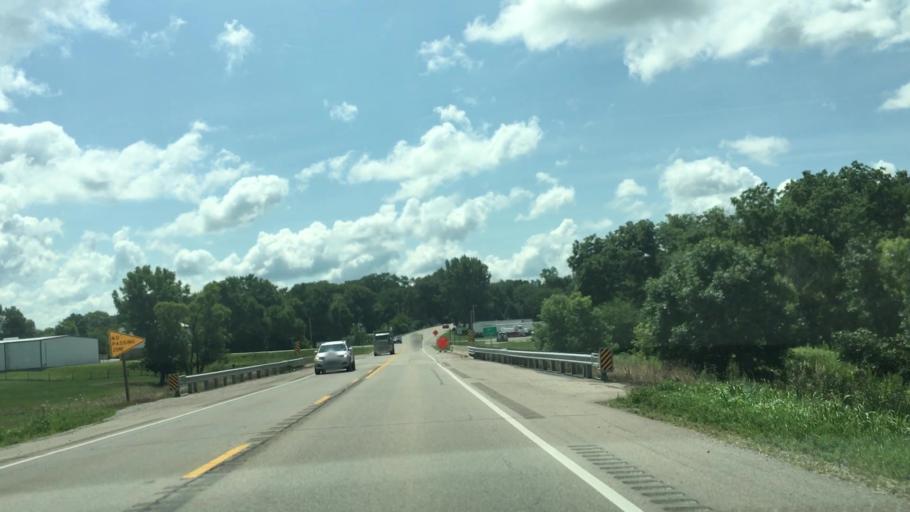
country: US
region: Iowa
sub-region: Johnson County
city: Solon
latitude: 41.8131
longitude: -91.4943
